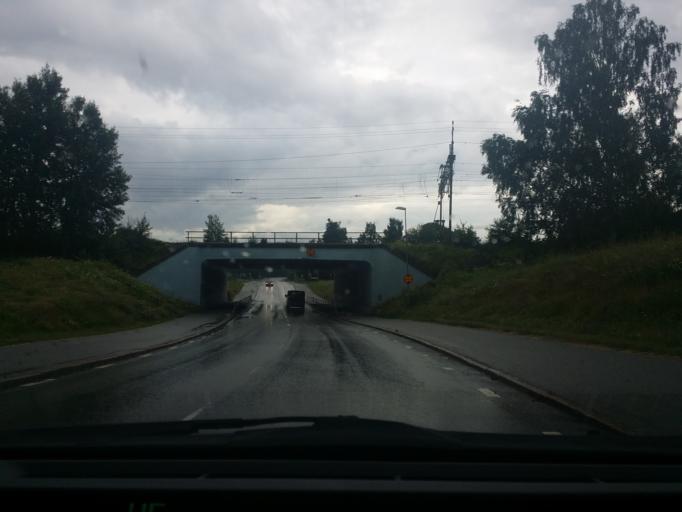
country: SE
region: OErebro
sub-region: Lindesbergs Kommun
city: Frovi
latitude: 59.4666
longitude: 15.3680
